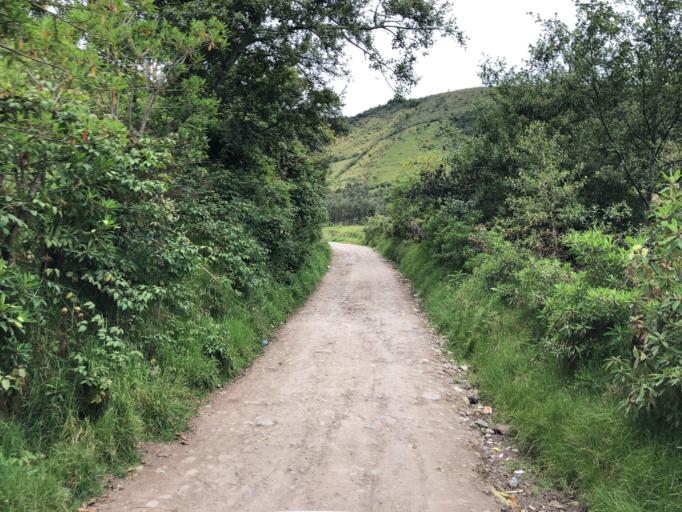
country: CO
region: Cauca
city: Totoro
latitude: 2.5114
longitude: -76.3729
